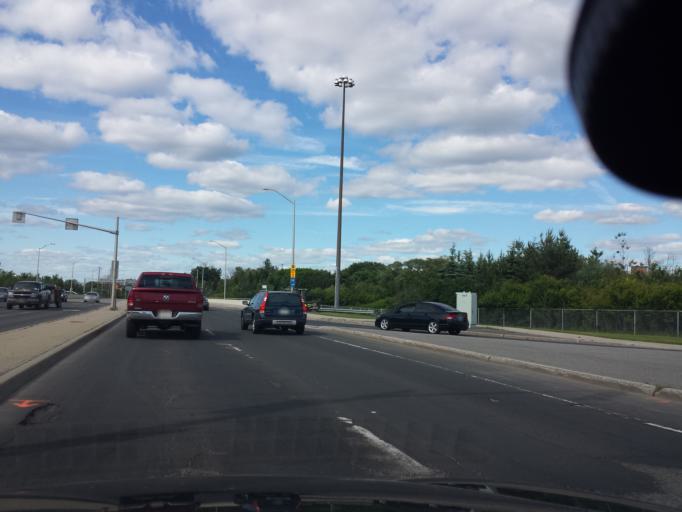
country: CA
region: Ontario
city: Bells Corners
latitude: 45.3343
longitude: -75.8130
